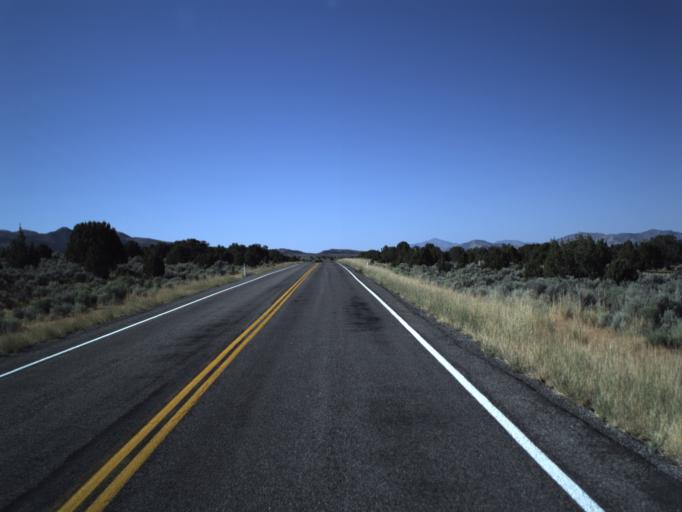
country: US
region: Utah
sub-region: Juab County
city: Mona
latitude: 39.8419
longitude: -112.1382
